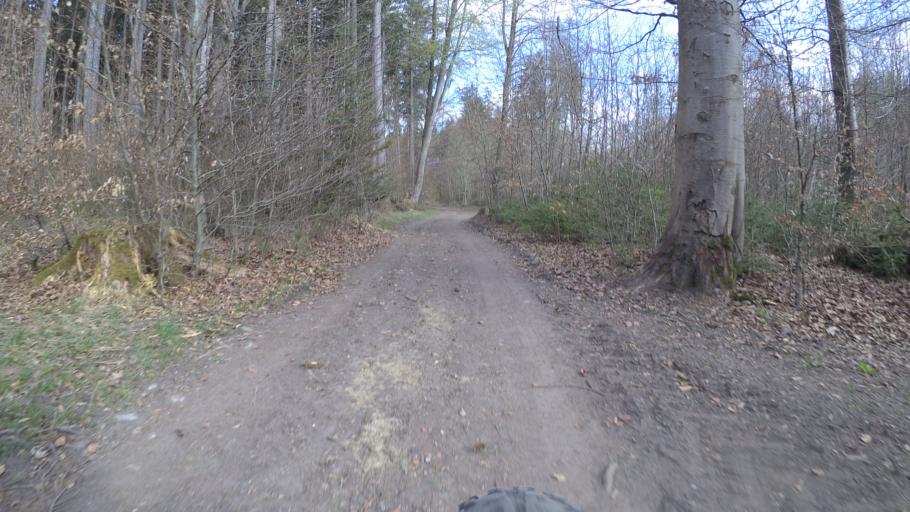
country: DE
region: Bavaria
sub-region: Upper Bavaria
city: Chieming
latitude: 47.9185
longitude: 12.5379
